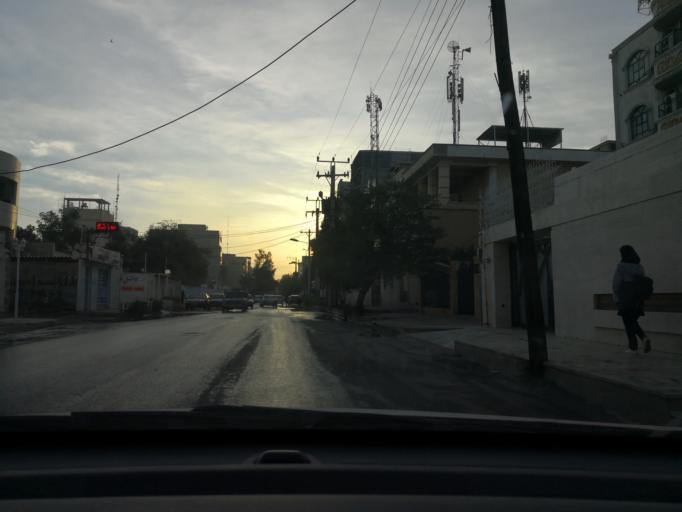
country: IR
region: Khuzestan
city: Ahvaz
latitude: 31.3520
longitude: 48.6804
